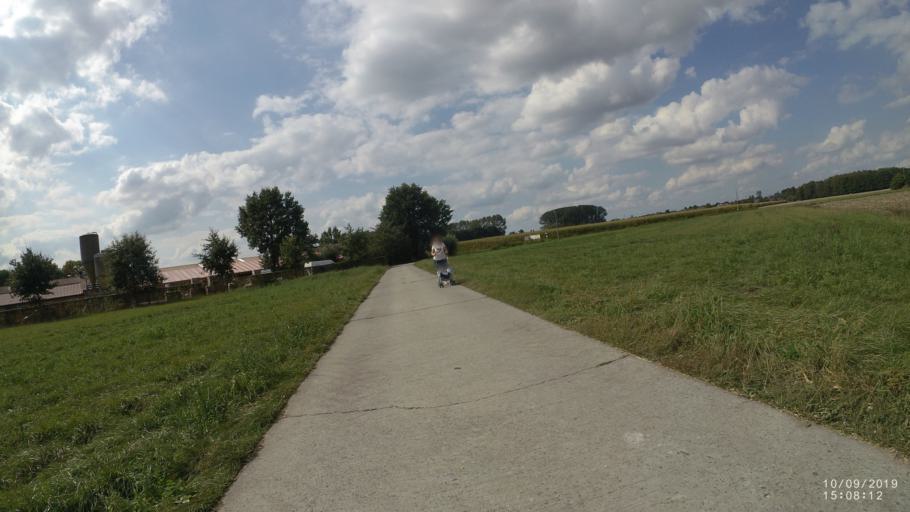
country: BE
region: Flanders
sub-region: Provincie Oost-Vlaanderen
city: Evergem
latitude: 51.1155
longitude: 3.6740
